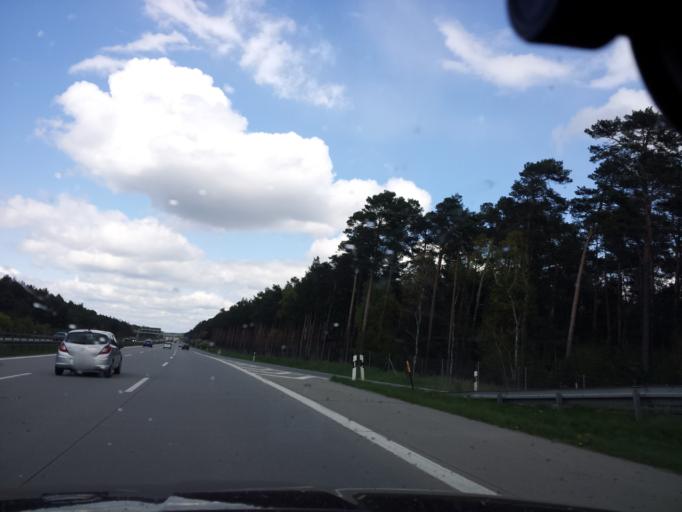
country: DE
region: Brandenburg
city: Grunheide
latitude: 52.3899
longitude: 13.7869
